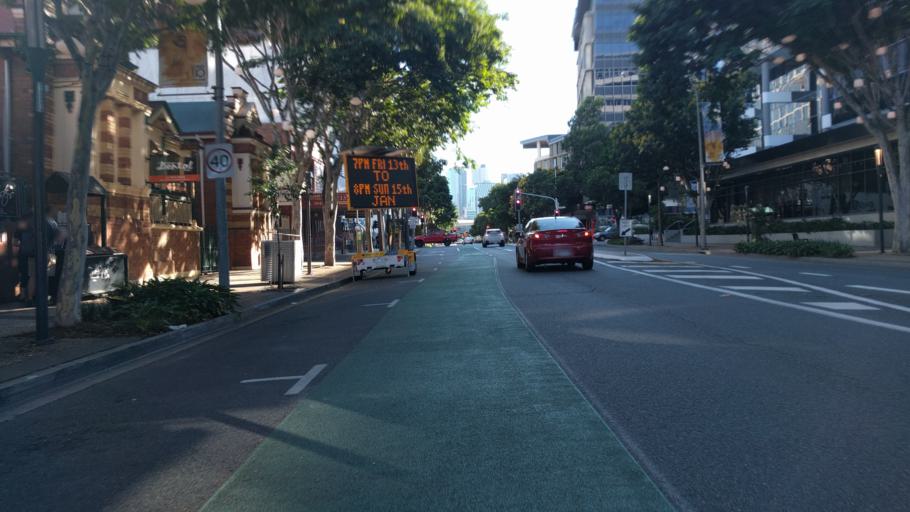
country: AU
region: Queensland
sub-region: Brisbane
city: South Brisbane
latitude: -27.4758
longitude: 153.0148
